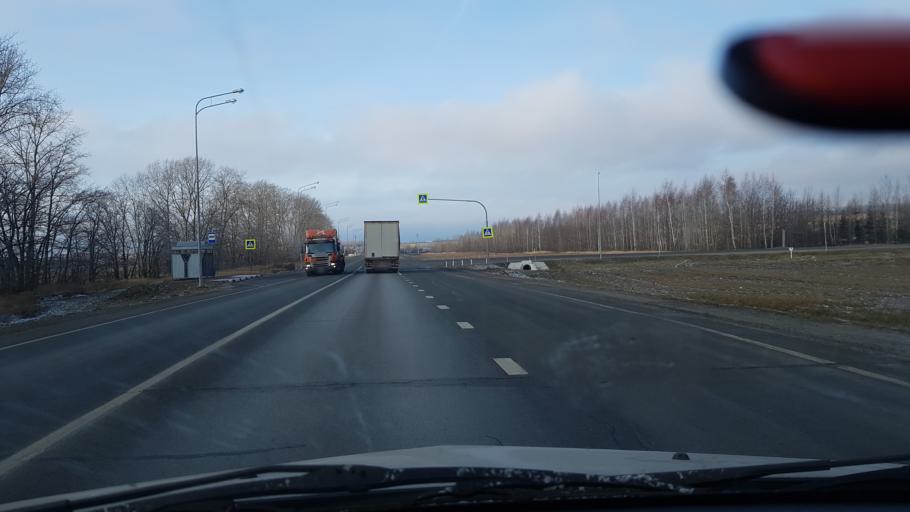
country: RU
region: Tatarstan
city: Laishevo
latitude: 55.3905
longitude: 49.8133
